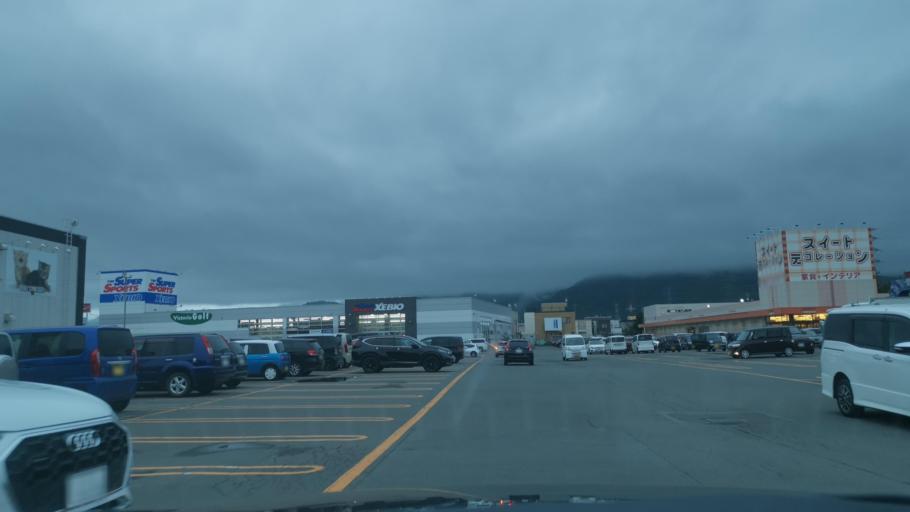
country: JP
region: Hokkaido
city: Sapporo
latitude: 43.1100
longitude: 141.2767
